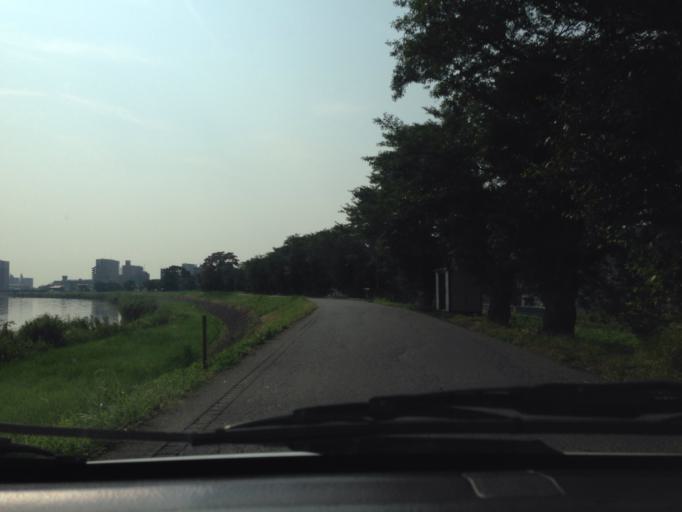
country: JP
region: Ibaraki
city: Naka
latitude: 36.0773
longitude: 140.1913
